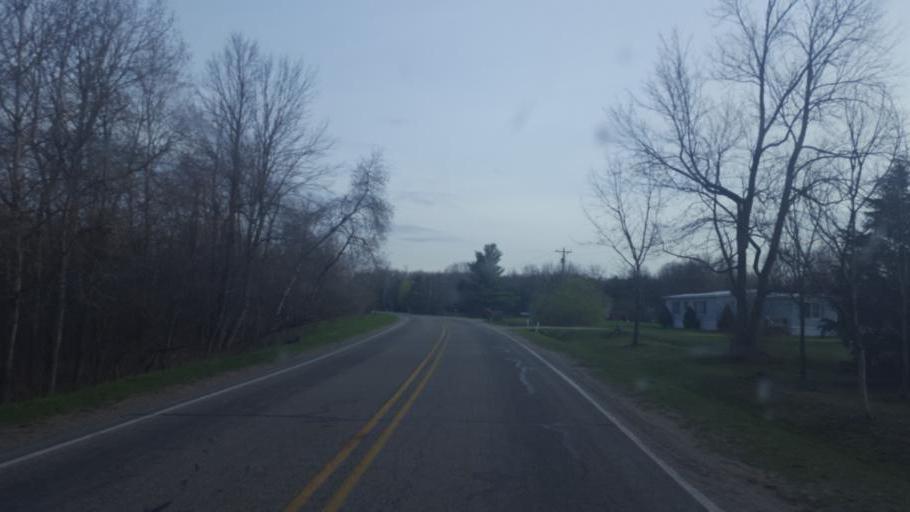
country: US
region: Michigan
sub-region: Isabella County
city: Lake Isabella
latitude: 43.5647
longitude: -84.9856
